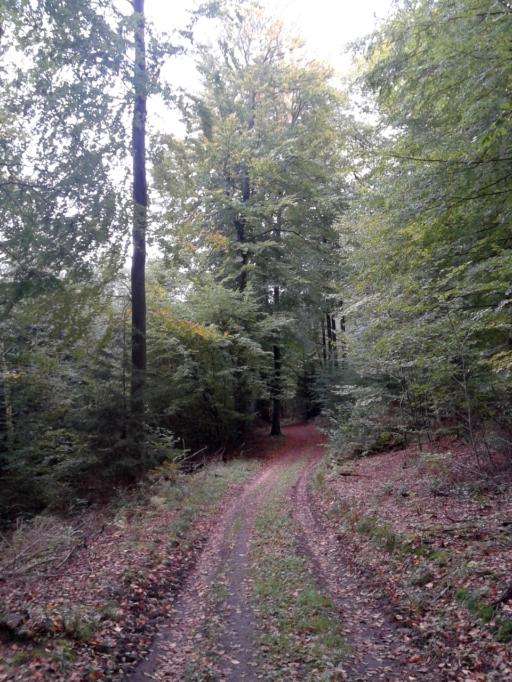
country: LU
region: Luxembourg
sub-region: Canton de Luxembourg
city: Sandweiler
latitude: 49.6430
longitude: 6.2019
